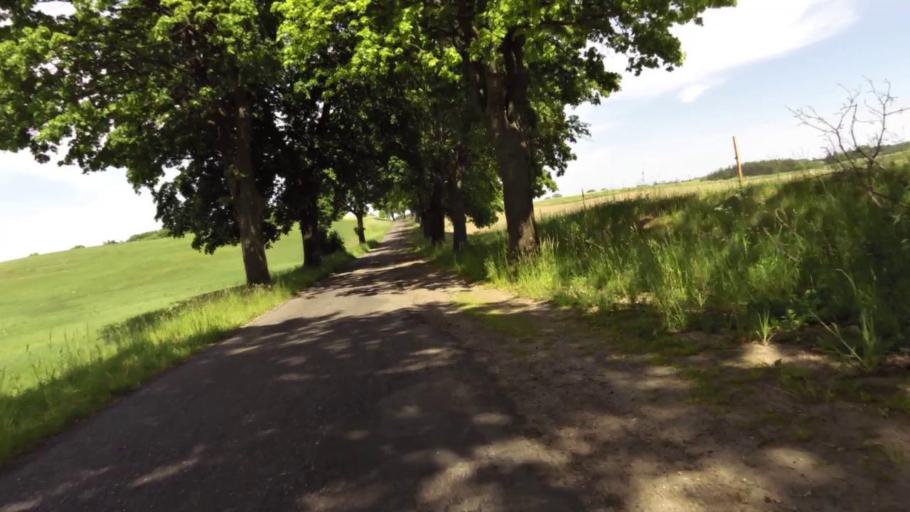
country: PL
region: West Pomeranian Voivodeship
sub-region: Powiat szczecinecki
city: Szczecinek
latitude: 53.6532
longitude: 16.6723
